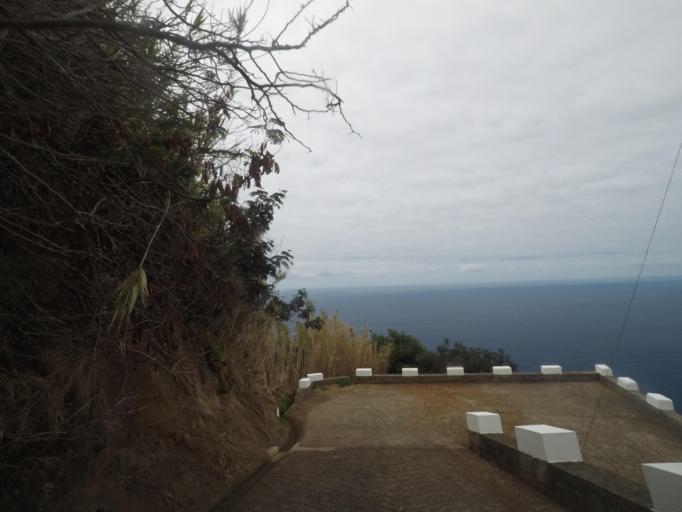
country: PT
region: Madeira
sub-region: Porto Moniz
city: Porto Moniz
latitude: 32.8643
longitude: -17.1794
